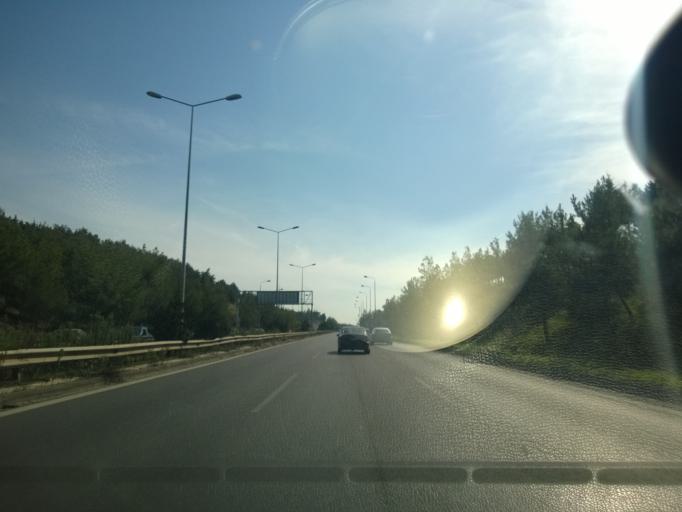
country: GR
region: Central Macedonia
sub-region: Nomos Thessalonikis
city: Agios Pavlos
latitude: 40.6482
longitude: 22.9675
